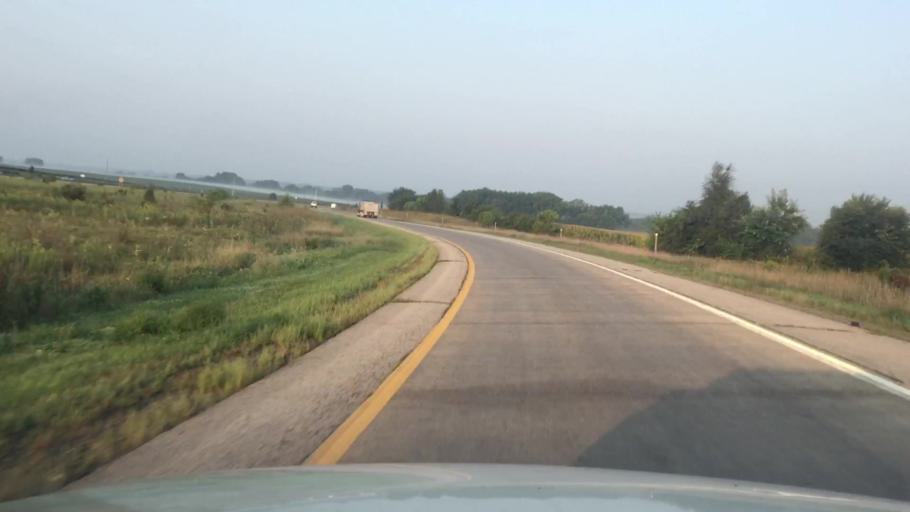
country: US
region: Iowa
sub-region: Polk County
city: Altoona
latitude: 41.6611
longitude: -93.5269
